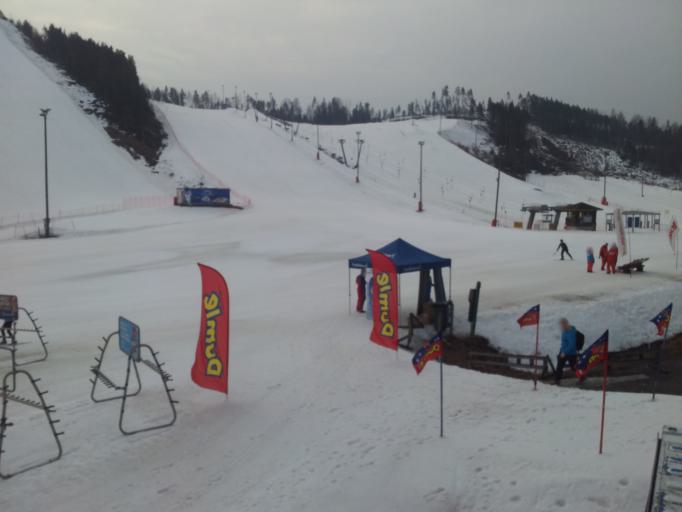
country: FI
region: Central Finland
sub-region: Jaemsae
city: Jaemsae
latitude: 61.8792
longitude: 25.2993
